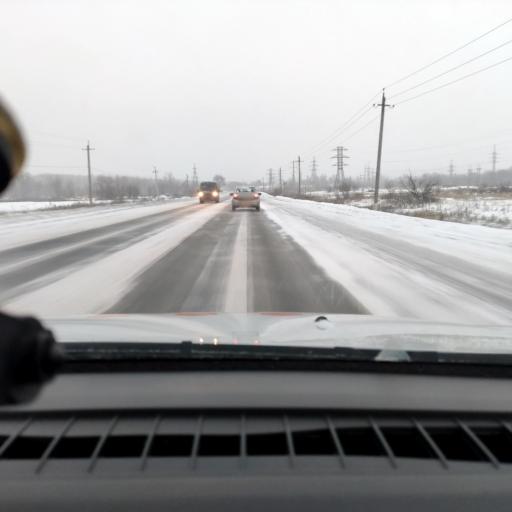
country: RU
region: Samara
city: Otradnyy
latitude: 53.3475
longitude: 51.3134
